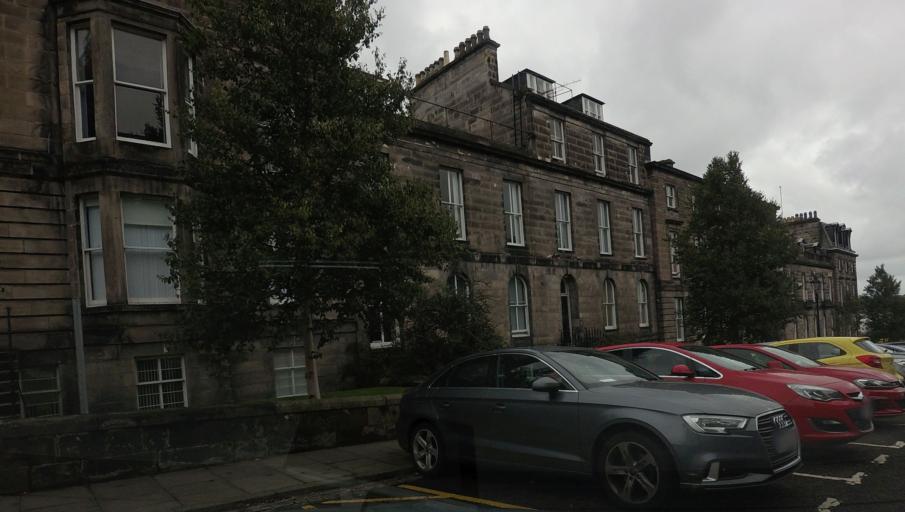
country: GB
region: Scotland
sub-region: Dundee City
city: Dundee
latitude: 56.4572
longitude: -2.9816
